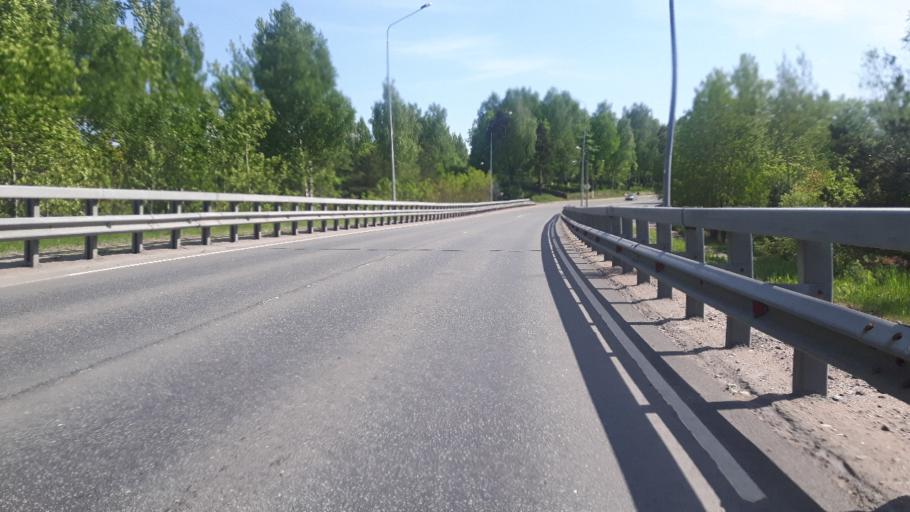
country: RU
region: Leningrad
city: Vyborg
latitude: 60.7349
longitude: 28.6976
